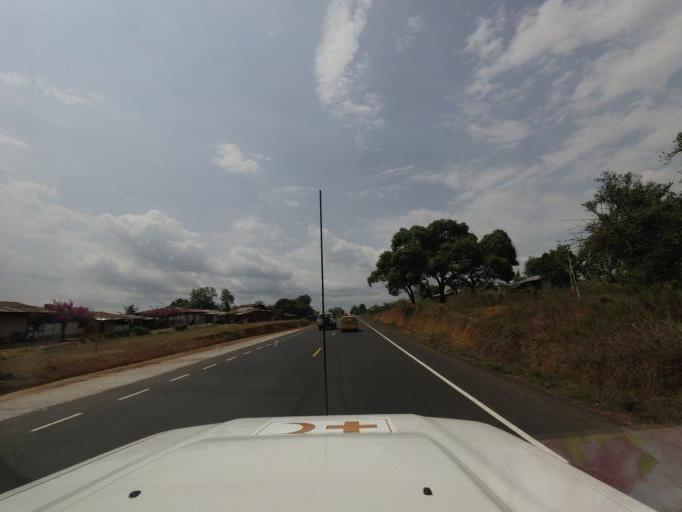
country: LR
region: Margibi
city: Kakata
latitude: 6.4801
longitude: -10.4027
